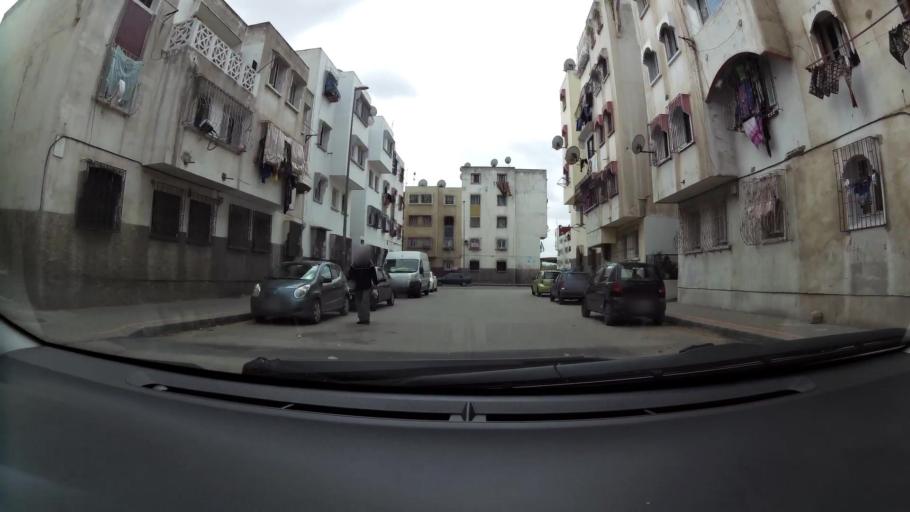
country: MA
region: Grand Casablanca
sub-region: Casablanca
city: Casablanca
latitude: 33.5925
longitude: -7.5567
